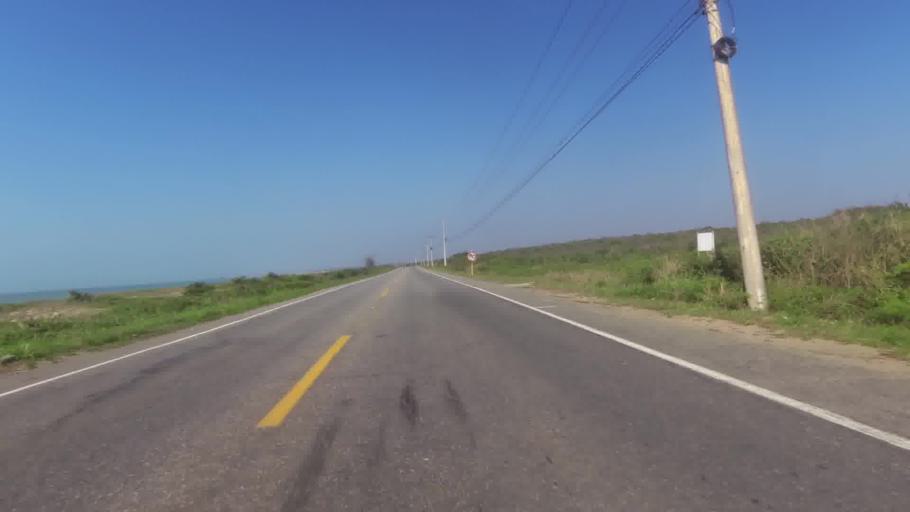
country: BR
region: Espirito Santo
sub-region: Itapemirim
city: Itapemirim
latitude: -20.9419
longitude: -40.8042
